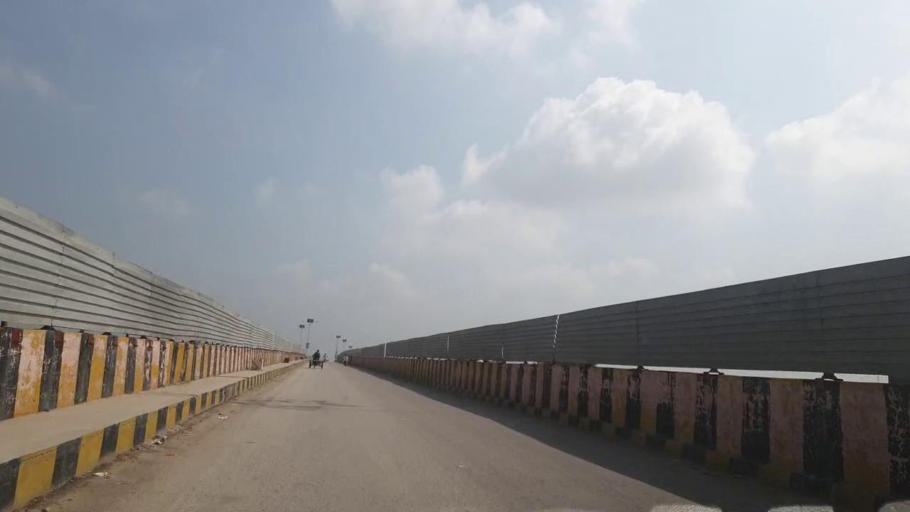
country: PK
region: Sindh
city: Khairpur
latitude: 27.5255
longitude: 68.7428
